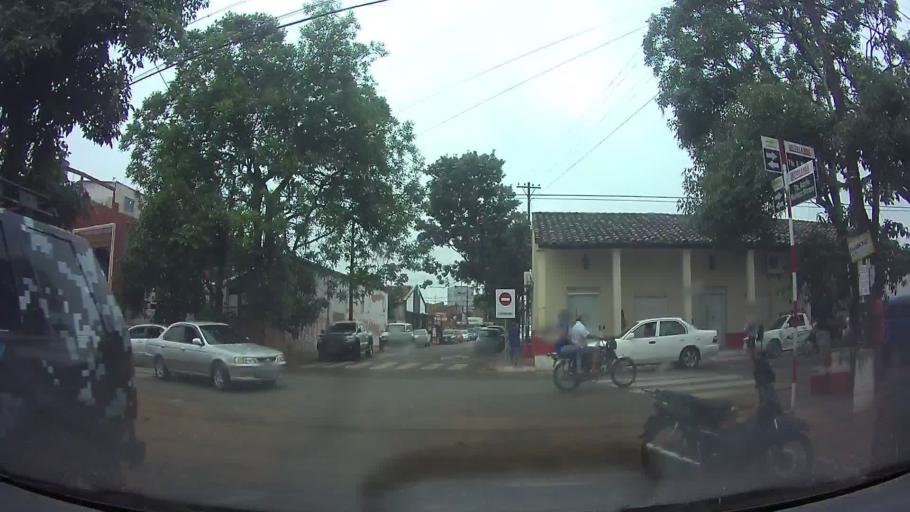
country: PY
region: Central
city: Itaugua
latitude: -25.3937
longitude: -57.3543
